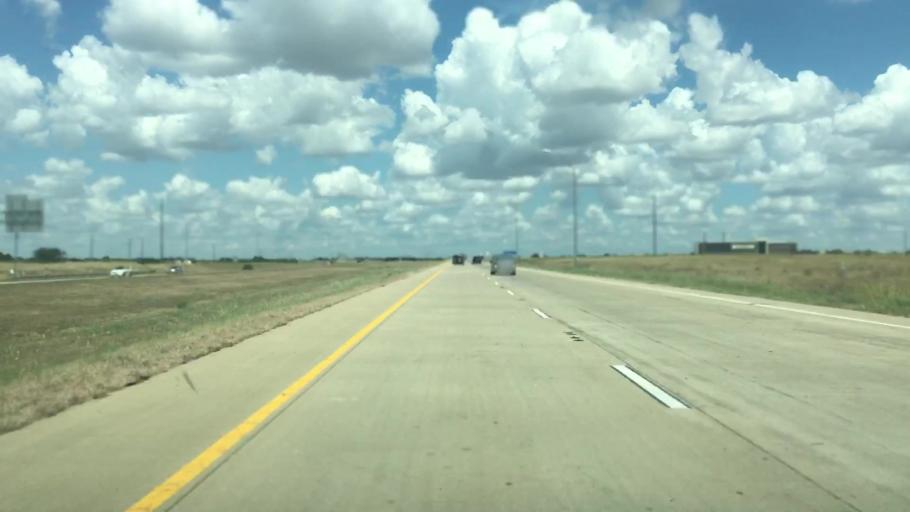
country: US
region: Texas
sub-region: Williamson County
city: Hutto
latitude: 30.5461
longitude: -97.5764
